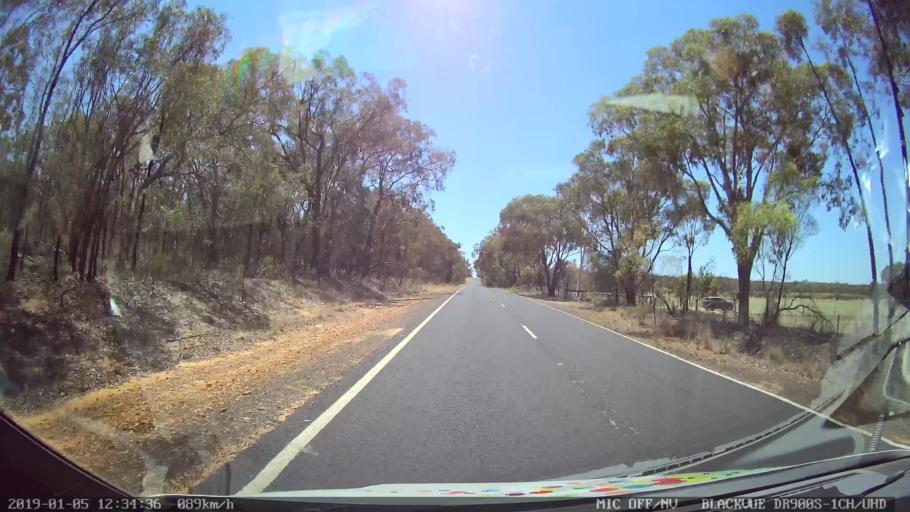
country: AU
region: New South Wales
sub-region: Warrumbungle Shire
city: Coonabarabran
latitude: -31.2117
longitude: 149.4129
